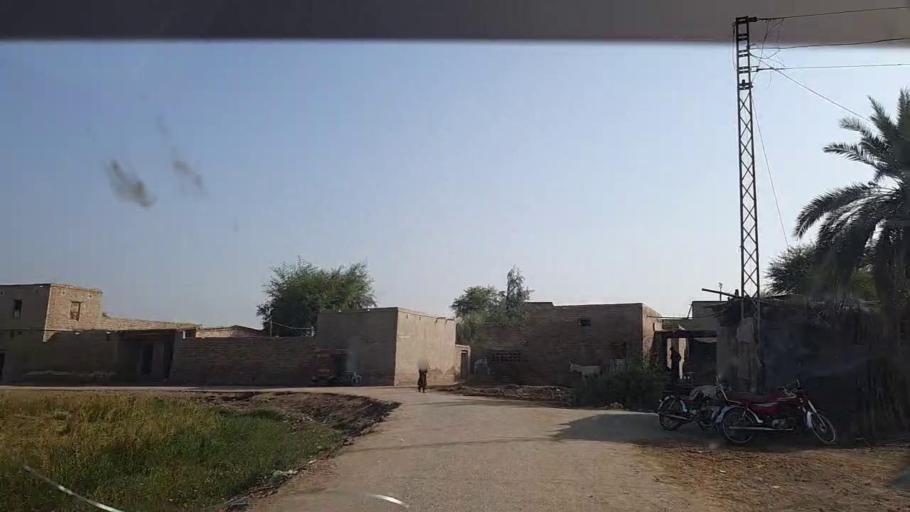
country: PK
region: Sindh
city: Shikarpur
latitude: 28.1166
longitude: 68.5808
